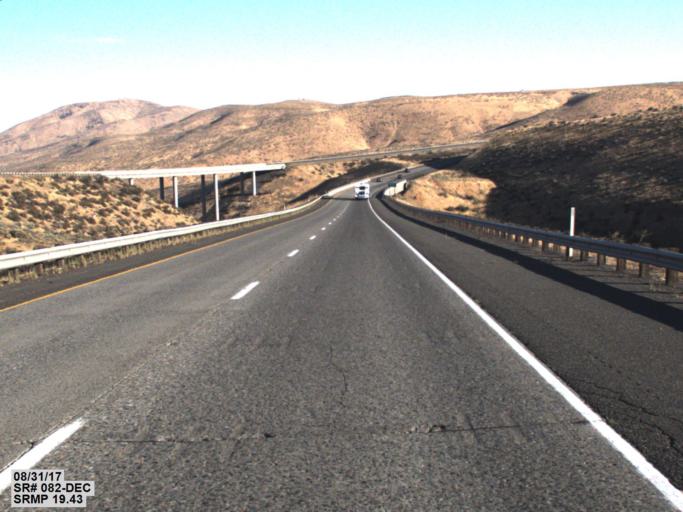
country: US
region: Washington
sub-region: Yakima County
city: Terrace Heights
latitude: 46.7439
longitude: -120.3879
